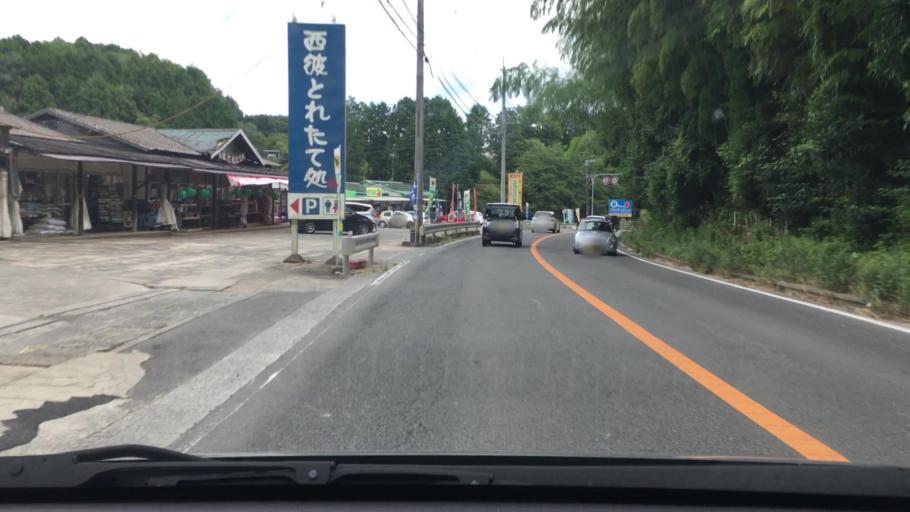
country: JP
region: Nagasaki
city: Togitsu
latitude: 32.9800
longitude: 129.7815
